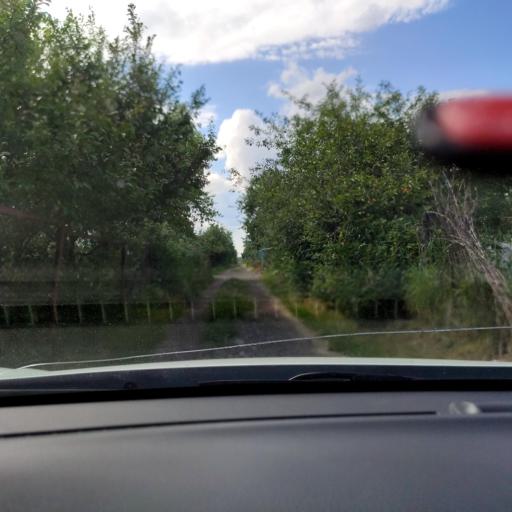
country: RU
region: Tatarstan
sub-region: Gorod Kazan'
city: Kazan
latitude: 55.8895
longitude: 49.0622
